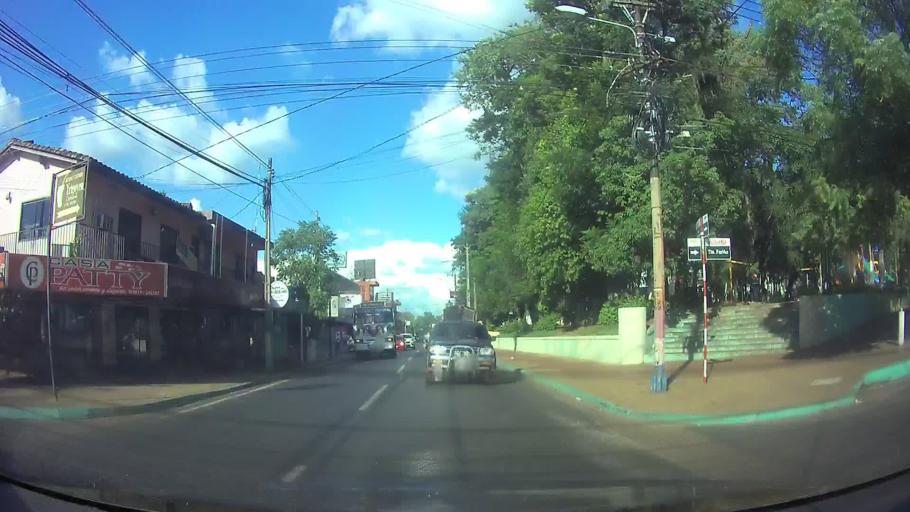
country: PY
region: Cordillera
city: Caacupe
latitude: -25.3860
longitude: -57.1432
